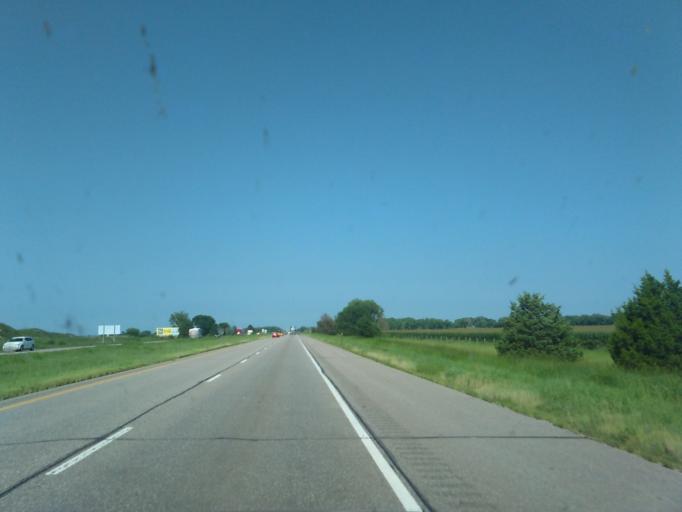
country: US
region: Nebraska
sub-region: Hall County
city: Wood River
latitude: 40.8024
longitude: -98.4789
